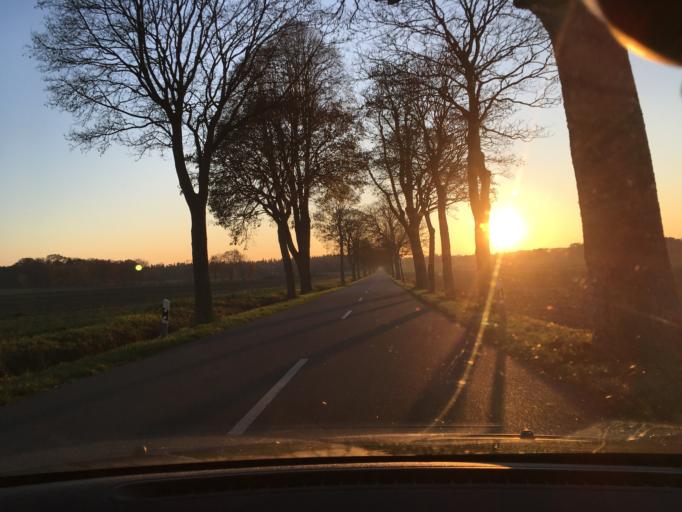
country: DE
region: Lower Saxony
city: Ebstorf
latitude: 53.0500
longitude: 10.4420
